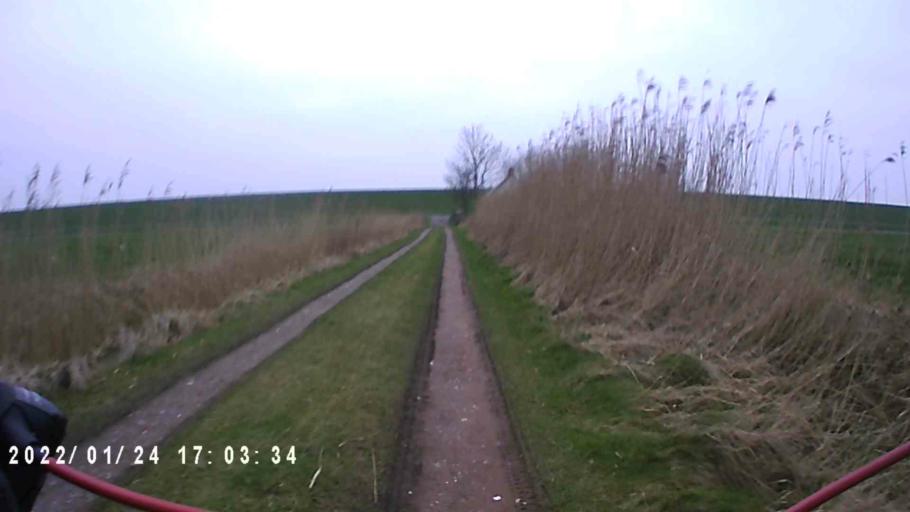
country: NL
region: Groningen
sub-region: Gemeente De Marne
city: Ulrum
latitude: 53.3942
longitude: 6.3193
